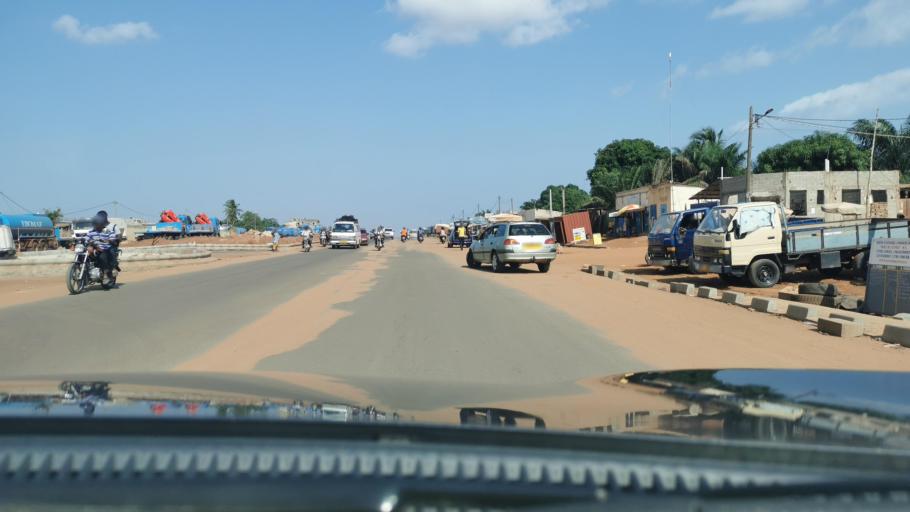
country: TG
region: Maritime
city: Lome
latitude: 6.2128
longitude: 1.1341
